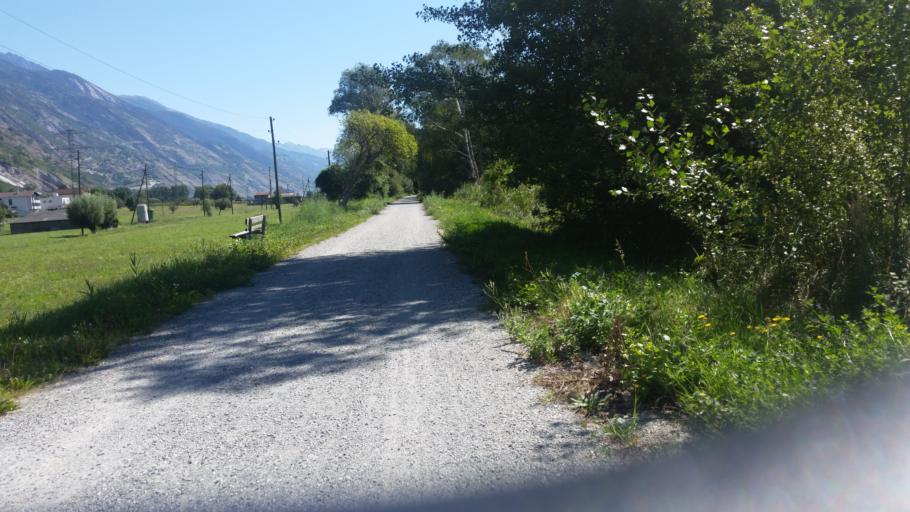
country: CH
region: Valais
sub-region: Leuk District
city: Turtmann
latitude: 46.3106
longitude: 7.7090
